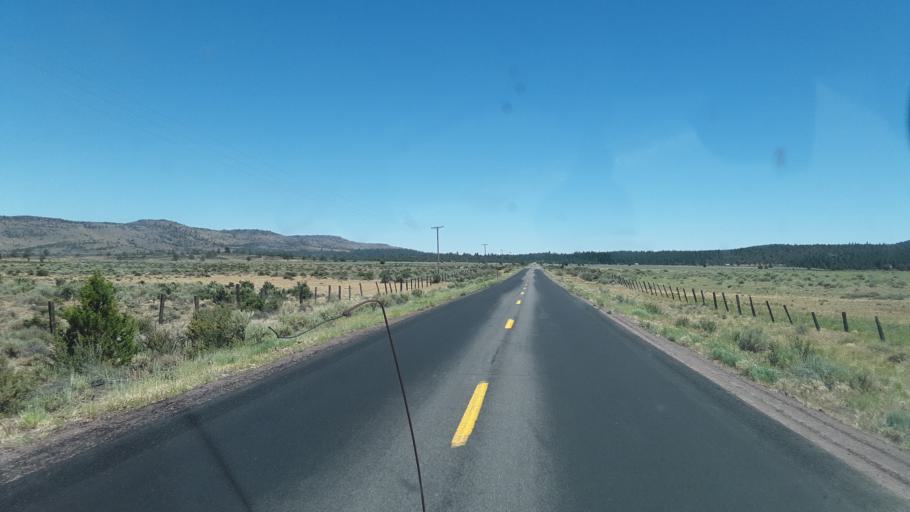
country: US
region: California
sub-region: Lassen County
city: Susanville
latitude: 40.5327
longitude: -120.6074
